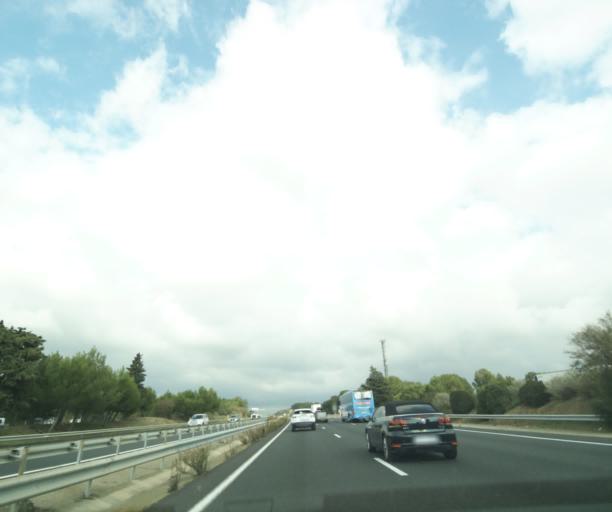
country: FR
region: Languedoc-Roussillon
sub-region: Departement de l'Herault
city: Lespignan
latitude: 43.2644
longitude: 3.1742
